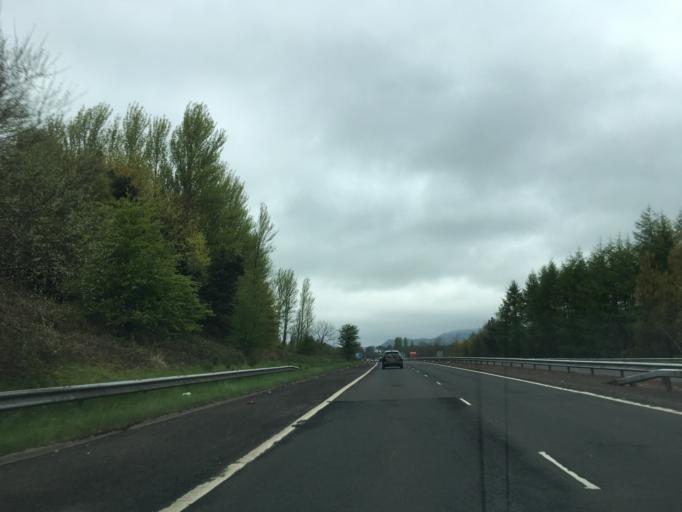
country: GB
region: Scotland
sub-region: Renfrewshire
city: Bishopton
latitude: 55.9003
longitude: -4.4847
